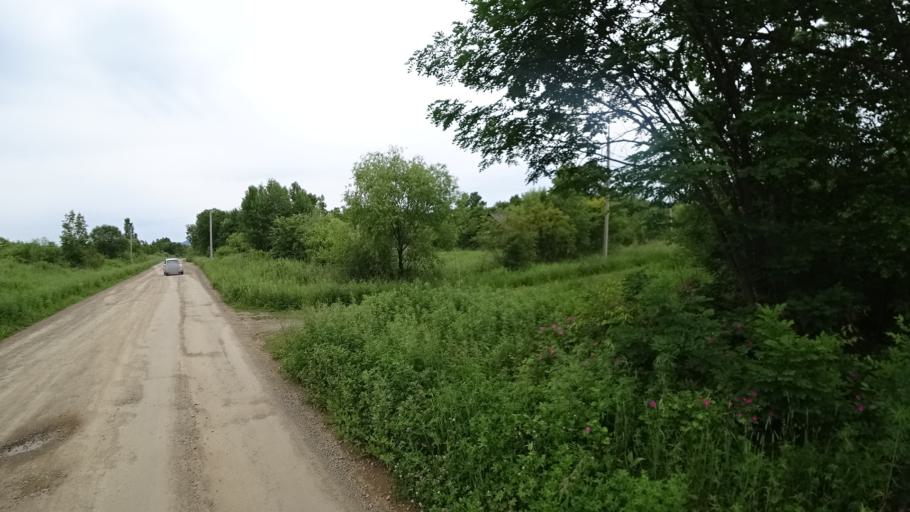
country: RU
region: Primorskiy
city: Arsen'yev
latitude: 44.1959
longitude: 133.3083
